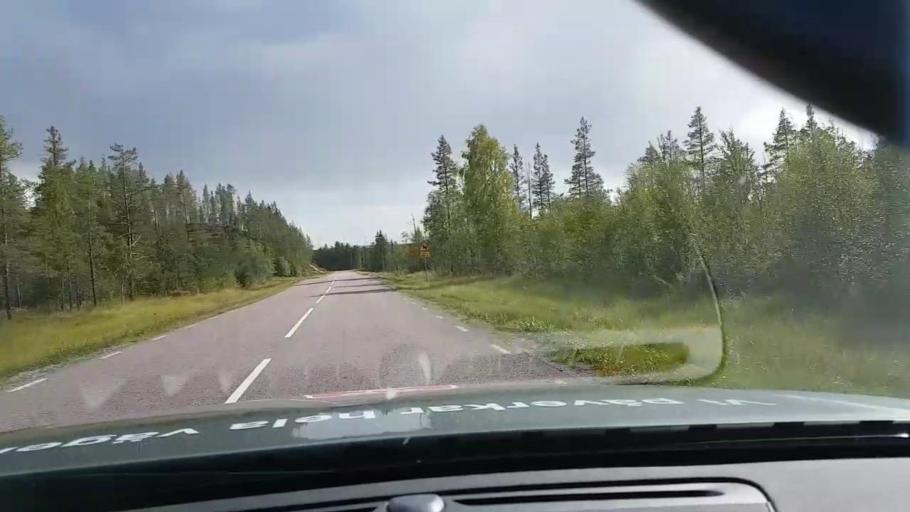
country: SE
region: Vaesterbotten
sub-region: Asele Kommun
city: Asele
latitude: 63.8703
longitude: 17.3577
